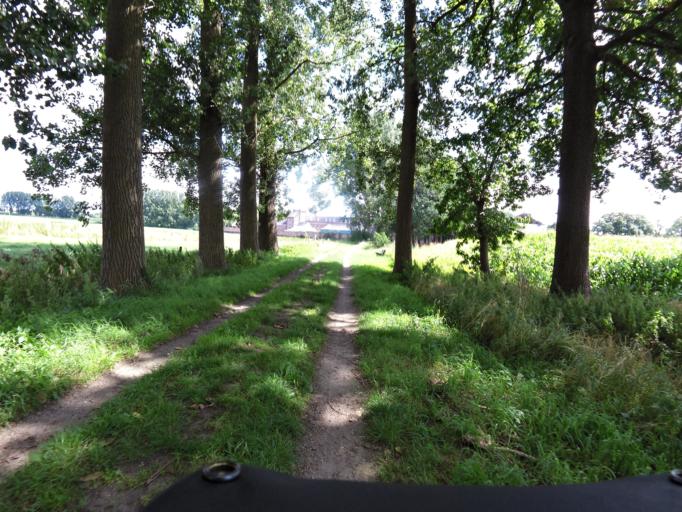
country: BE
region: Flanders
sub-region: Provincie Antwerpen
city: Hoogstraten
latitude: 51.4050
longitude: 4.7784
